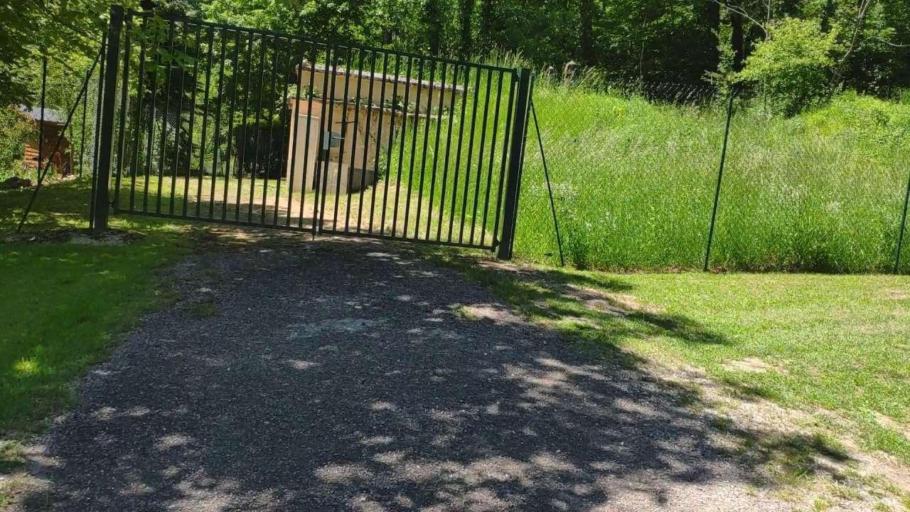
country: FR
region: Franche-Comte
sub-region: Departement du Jura
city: Poligny
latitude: 46.7628
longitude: 5.6804
